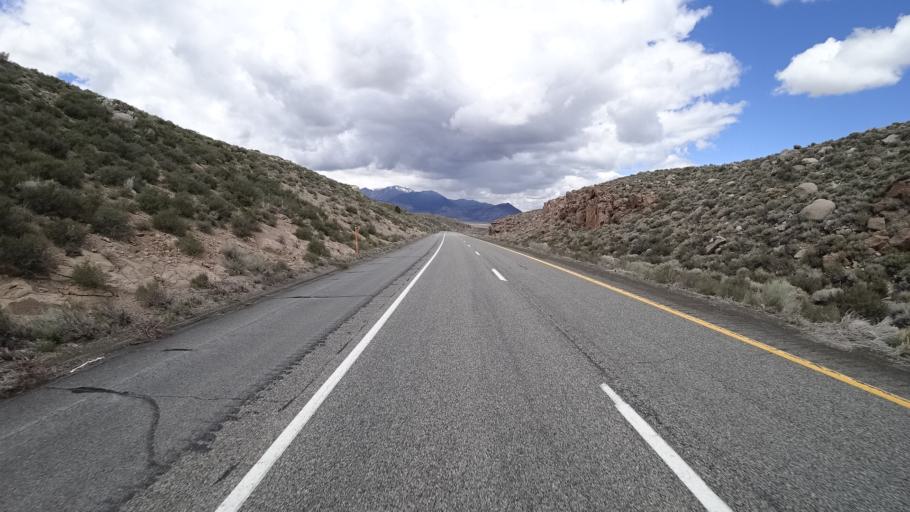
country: US
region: California
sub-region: Mono County
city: Mammoth Lakes
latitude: 37.8491
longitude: -119.0811
